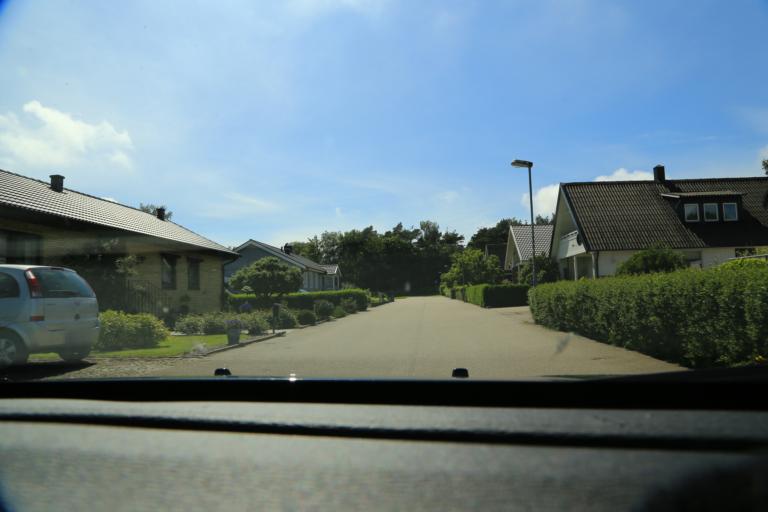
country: SE
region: Halland
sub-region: Varbergs Kommun
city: Varberg
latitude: 57.1054
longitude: 12.2892
